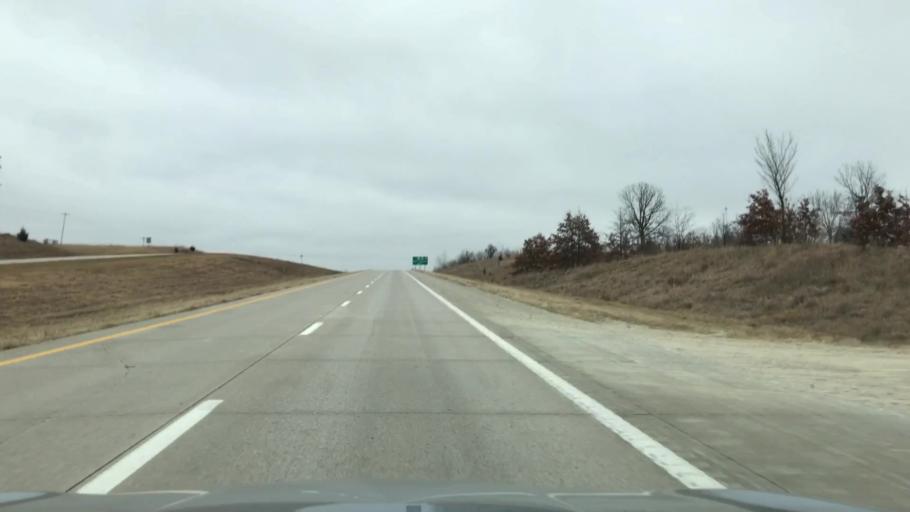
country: US
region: Missouri
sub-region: Linn County
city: Marceline
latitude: 39.7650
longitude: -92.7592
